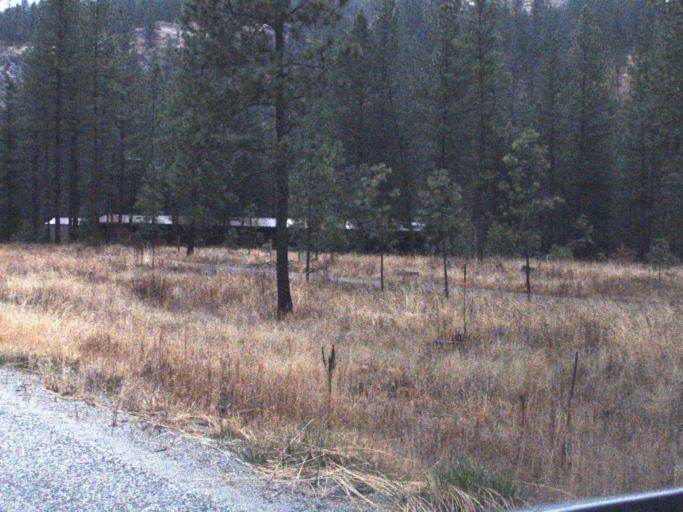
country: US
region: Washington
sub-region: Stevens County
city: Kettle Falls
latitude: 48.7860
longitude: -118.1489
